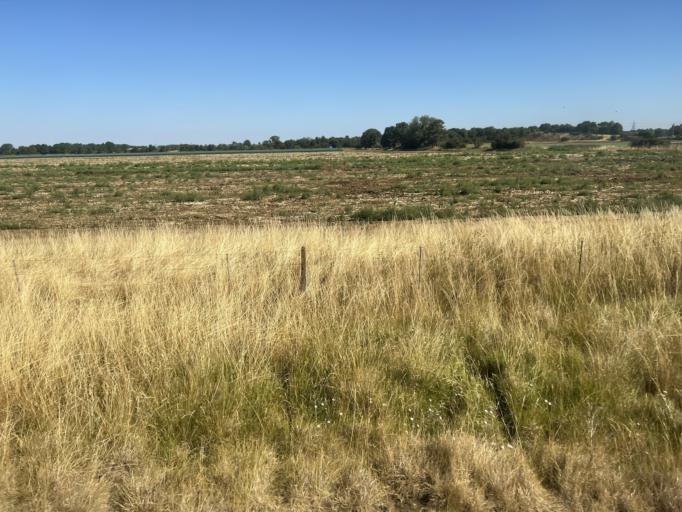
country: GB
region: England
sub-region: Lincolnshire
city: Sleaford
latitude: 52.9916
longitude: -0.3686
